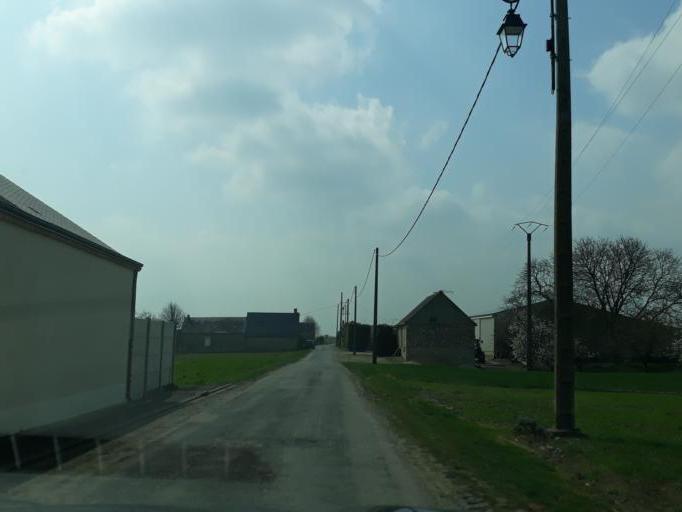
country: FR
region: Centre
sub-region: Departement d'Eure-et-Loir
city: Baigneaux
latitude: 48.0916
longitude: 1.8206
